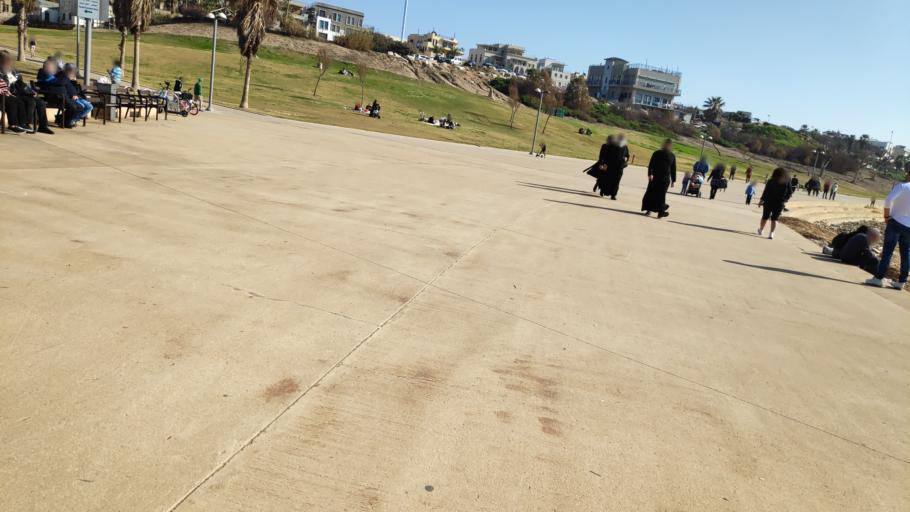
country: IL
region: Tel Aviv
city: Yafo
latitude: 32.0445
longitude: 34.7462
